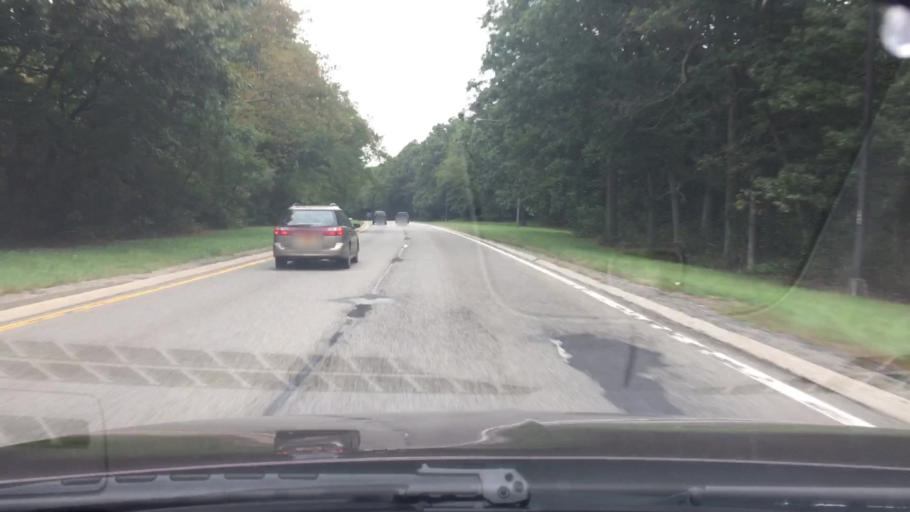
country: US
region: New York
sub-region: Suffolk County
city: South Huntington
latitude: 40.8166
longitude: -73.3728
